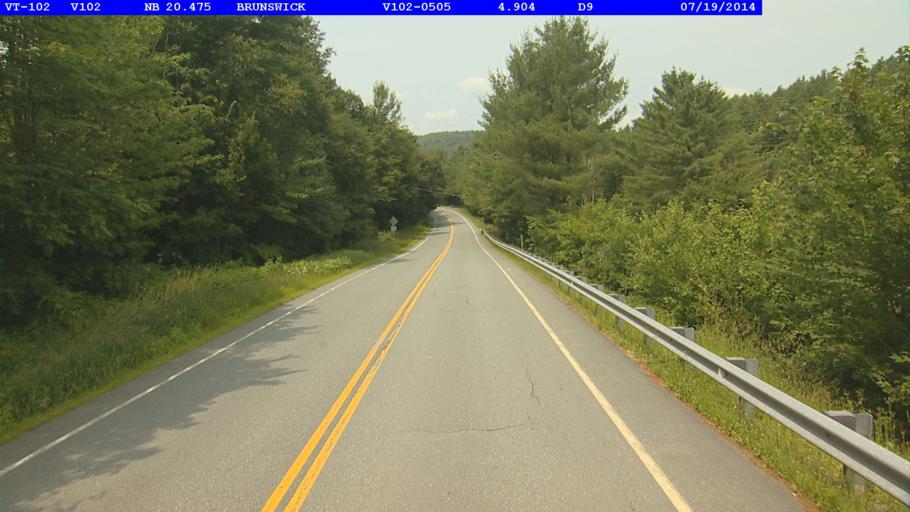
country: US
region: New Hampshire
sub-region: Coos County
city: Stratford
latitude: 44.7232
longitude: -71.6250
